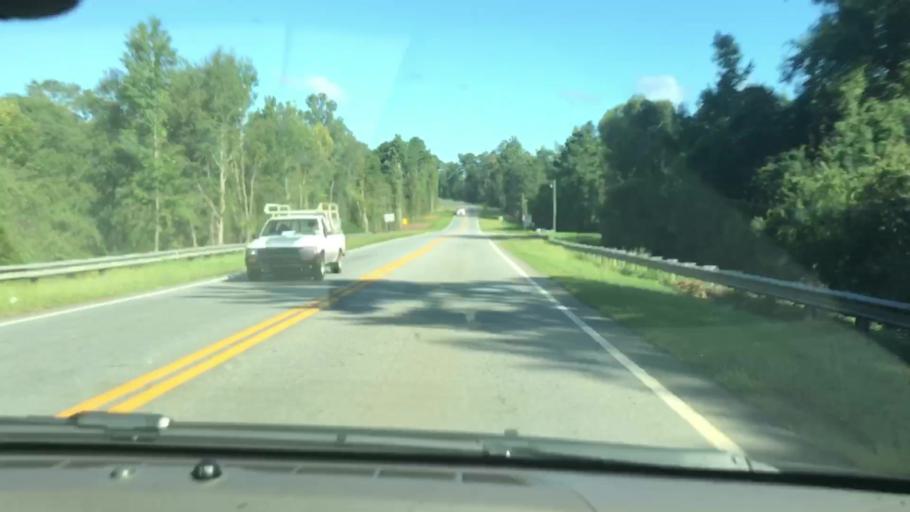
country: US
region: Georgia
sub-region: Quitman County
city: Georgetown
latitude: 31.8753
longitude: -85.0811
